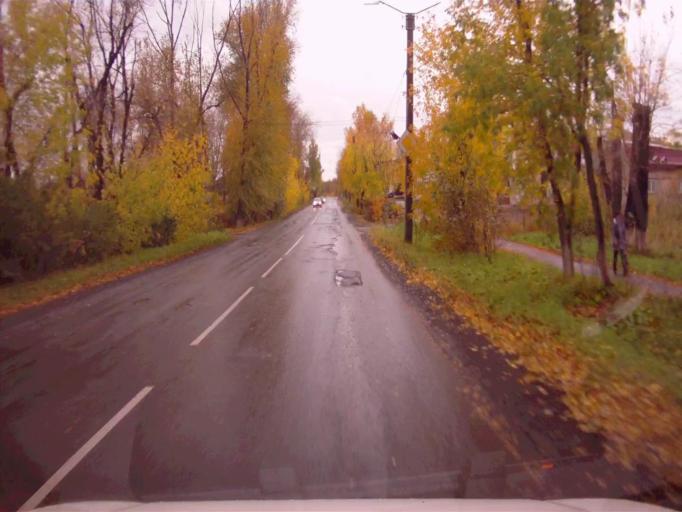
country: RU
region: Chelyabinsk
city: Verkhniy Ufaley
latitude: 56.0392
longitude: 60.2542
